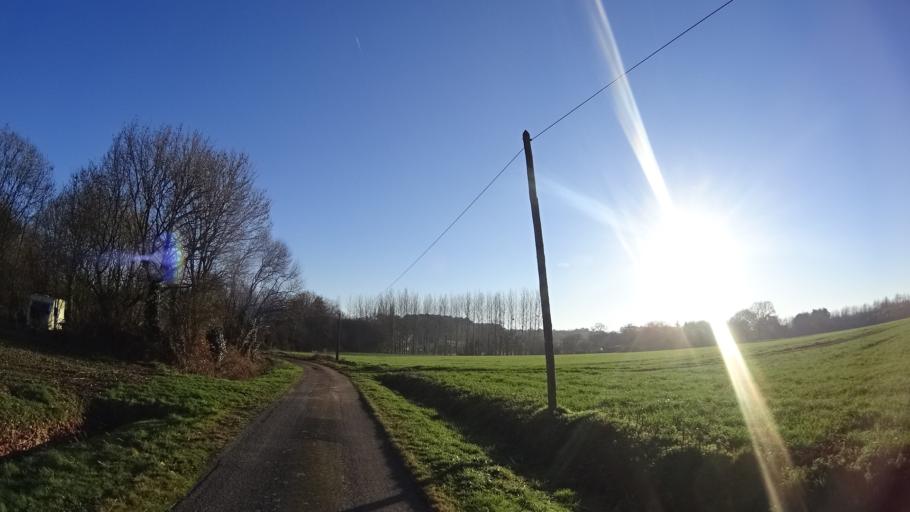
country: FR
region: Brittany
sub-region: Departement du Morbihan
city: Allaire
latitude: 47.6537
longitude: -2.1615
